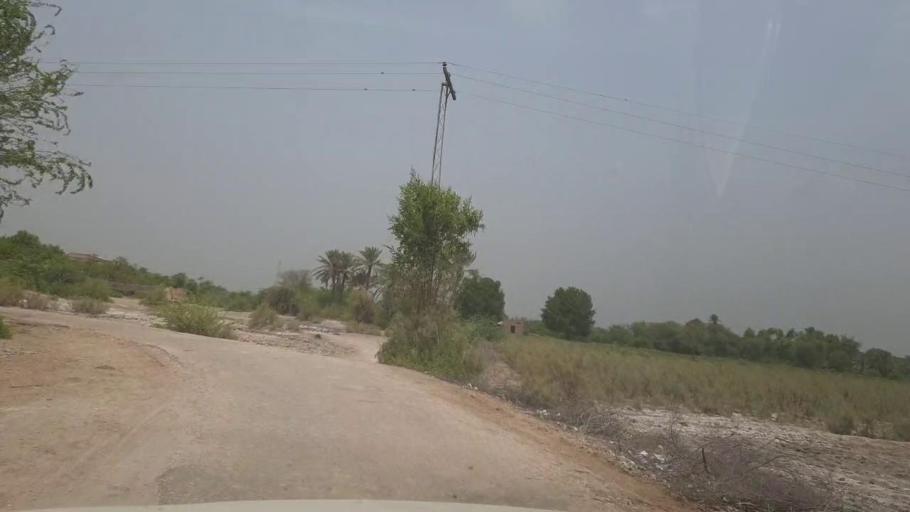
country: PK
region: Sindh
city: Kot Diji
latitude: 27.4403
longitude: 68.6458
